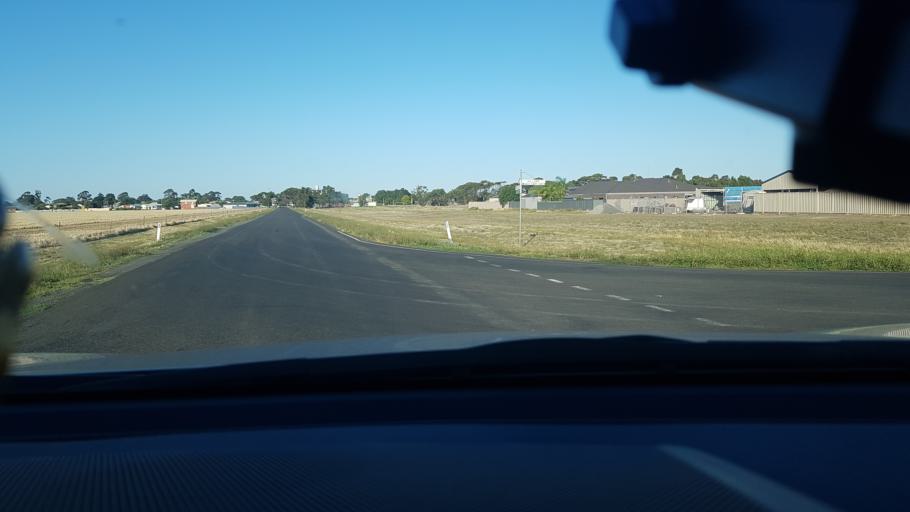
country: AU
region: Victoria
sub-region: Horsham
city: Horsham
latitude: -36.7114
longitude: 142.1784
